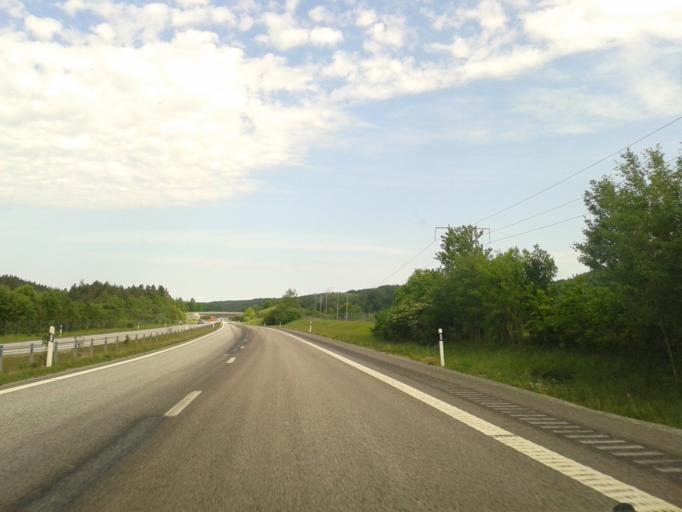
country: SE
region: Vaestra Goetaland
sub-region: Munkedals Kommun
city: Munkedal
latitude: 58.5272
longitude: 11.5439
